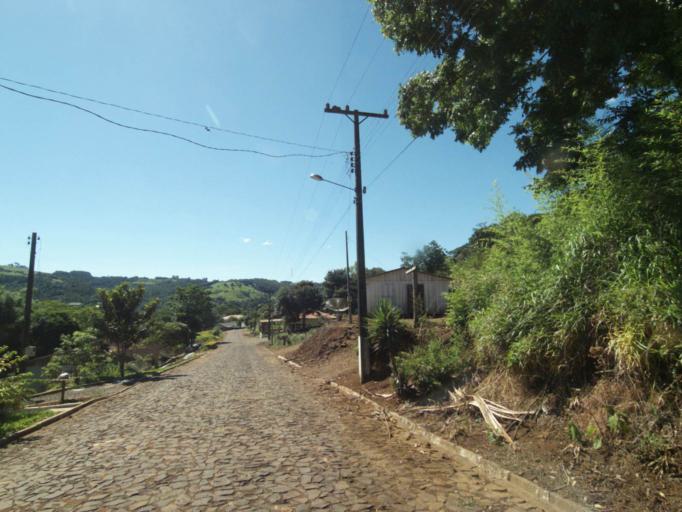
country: BR
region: Parana
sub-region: Ampere
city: Ampere
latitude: -26.1724
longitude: -53.3581
